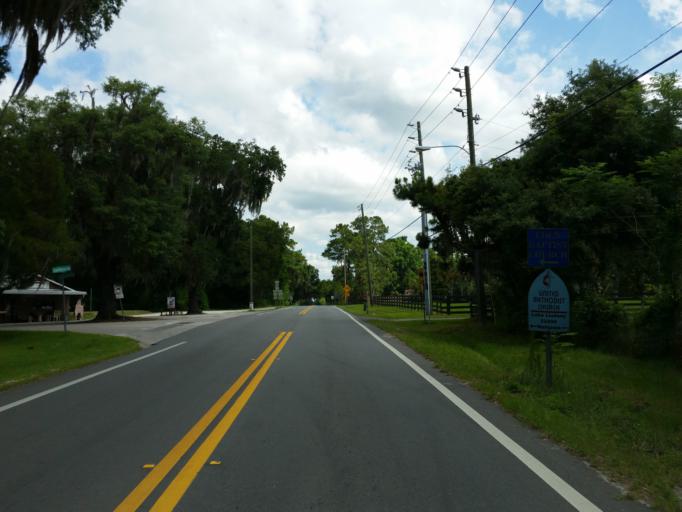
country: US
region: Florida
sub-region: Hernando County
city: North Brooksville
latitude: 28.6346
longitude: -82.3596
